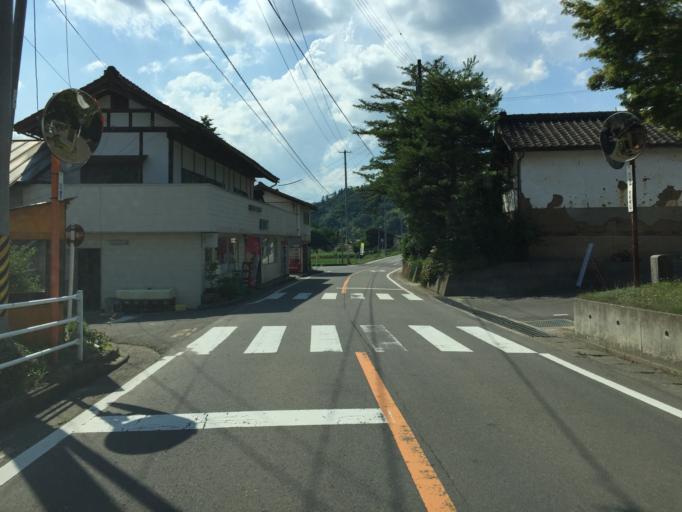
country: JP
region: Fukushima
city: Yanagawamachi-saiwaicho
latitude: 37.8024
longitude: 140.6327
